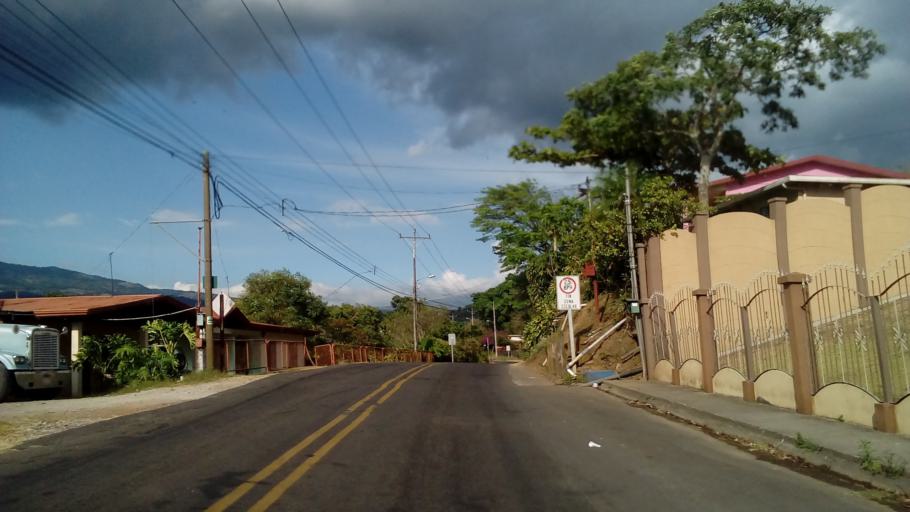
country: CR
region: Alajuela
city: Carrillos
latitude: 10.0741
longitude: -84.2740
